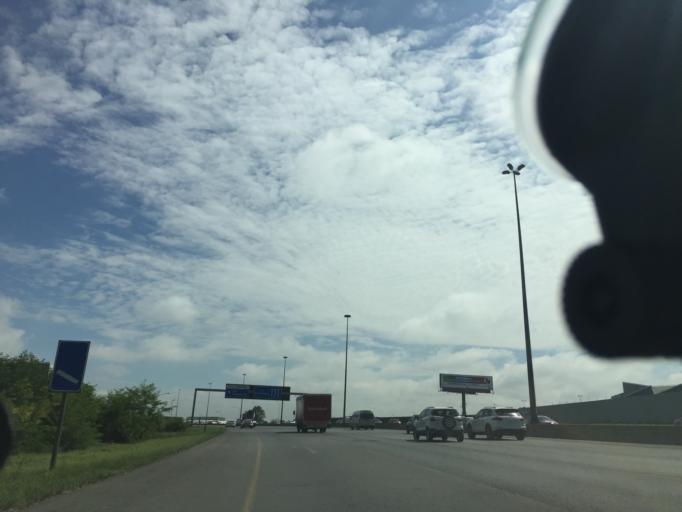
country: ZA
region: Gauteng
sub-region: City of Johannesburg Metropolitan Municipality
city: Modderfontein
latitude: -26.0956
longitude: 28.0838
